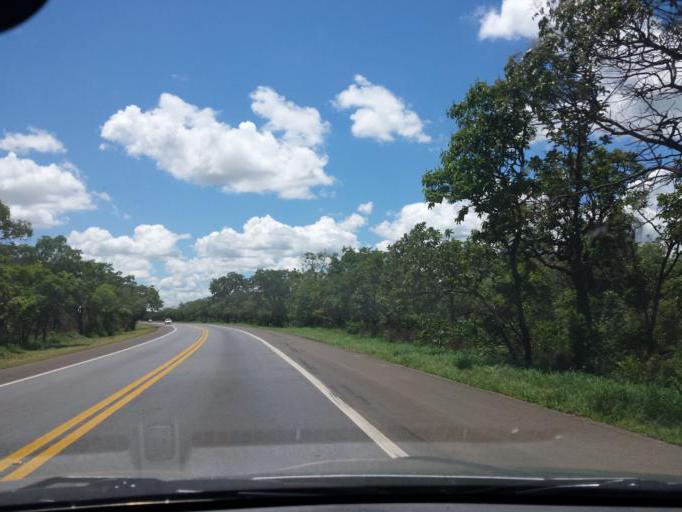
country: BR
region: Goias
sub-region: Cristalina
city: Cristalina
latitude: -16.6500
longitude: -47.7372
